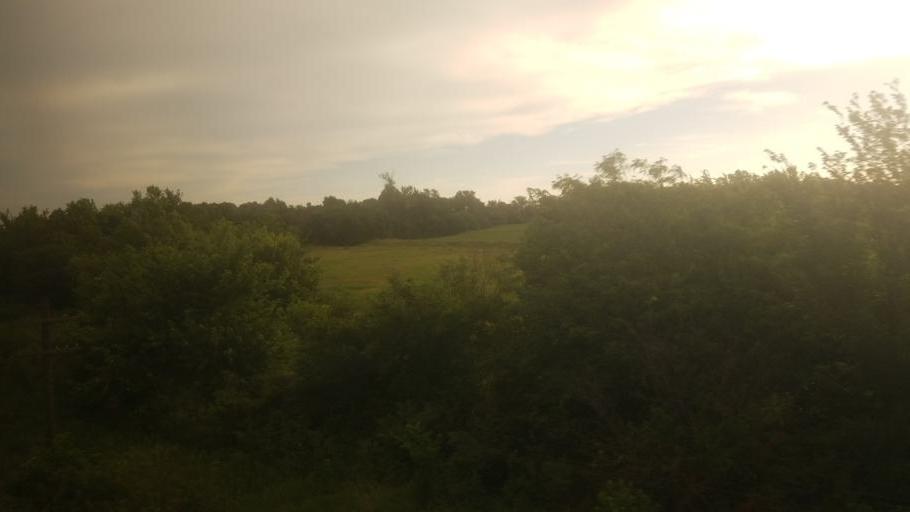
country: US
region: Kansas
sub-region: Osage County
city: Carbondale
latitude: 38.8461
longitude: -95.6979
